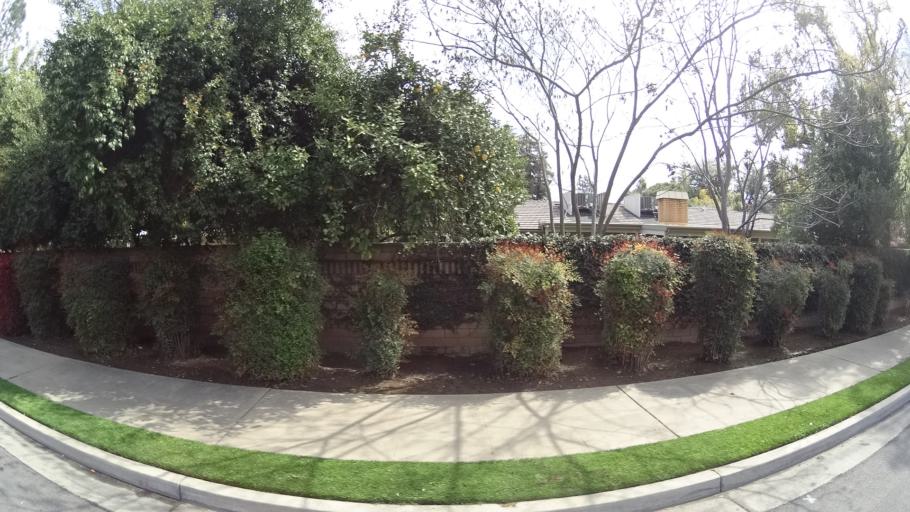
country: US
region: California
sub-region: Fresno County
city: Fresno
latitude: 36.8424
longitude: -119.8566
